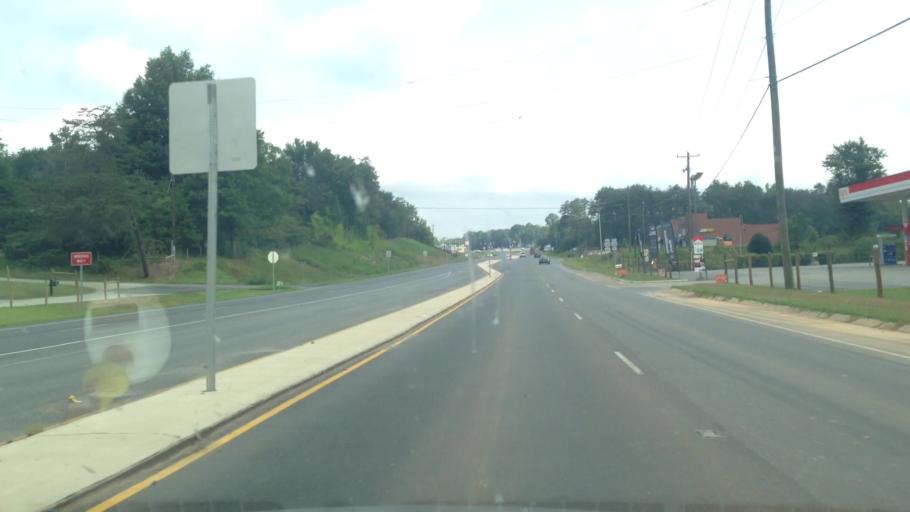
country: US
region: North Carolina
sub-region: Guilford County
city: Summerfield
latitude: 36.1864
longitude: -79.8892
